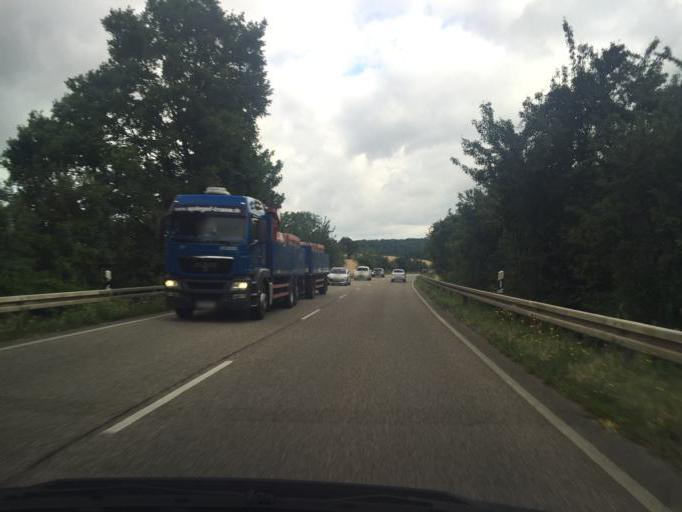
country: DE
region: Baden-Wuerttemberg
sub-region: Karlsruhe Region
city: Bruchsal
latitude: 49.1030
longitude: 8.6375
